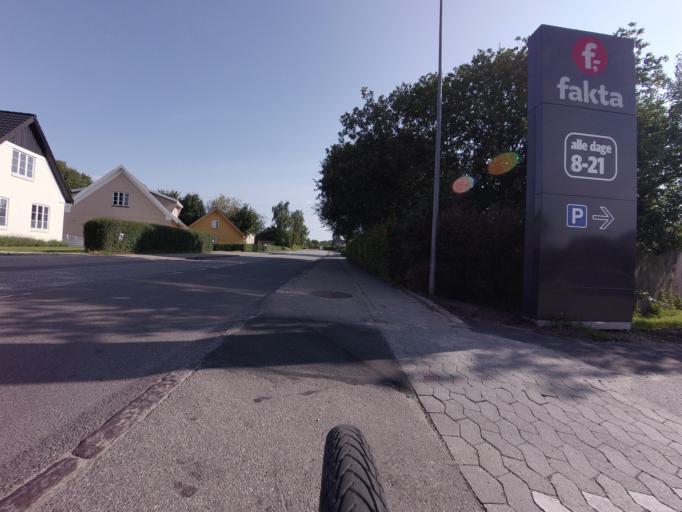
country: DK
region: Zealand
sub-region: Soro Kommune
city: Soro
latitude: 55.4542
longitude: 11.5584
